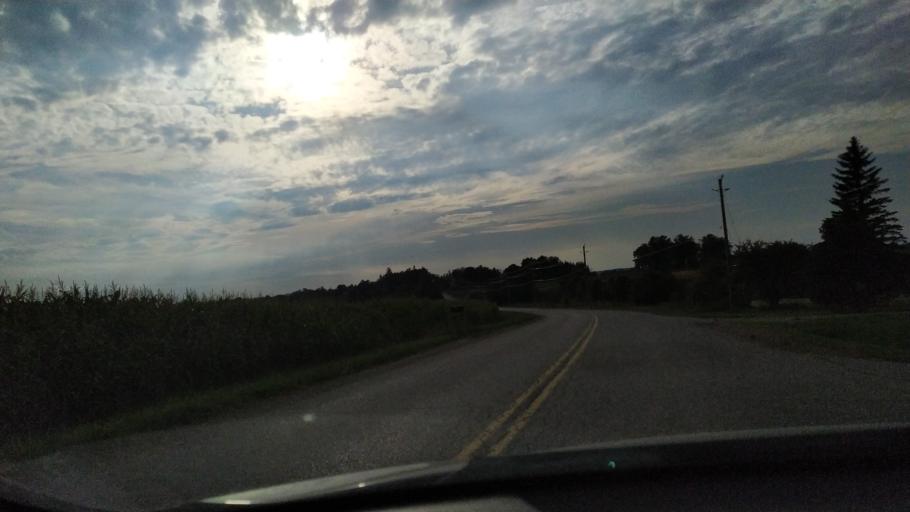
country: CA
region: Ontario
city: Stratford
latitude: 43.4633
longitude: -80.7766
